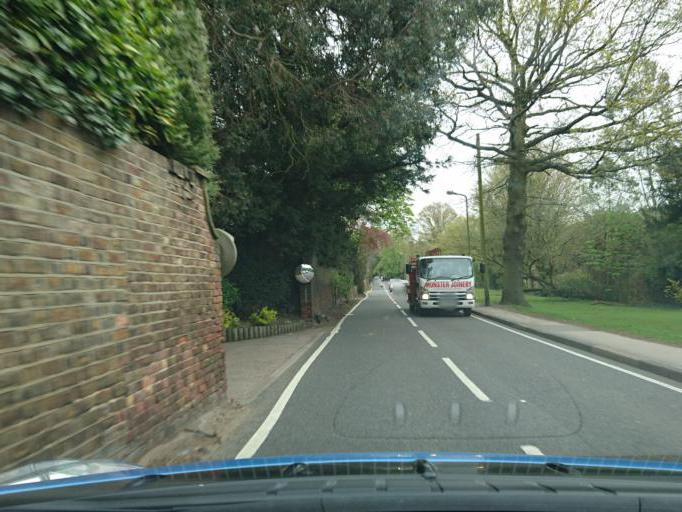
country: GB
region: England
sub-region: Greater London
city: Barnet
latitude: 51.6342
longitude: -0.1999
